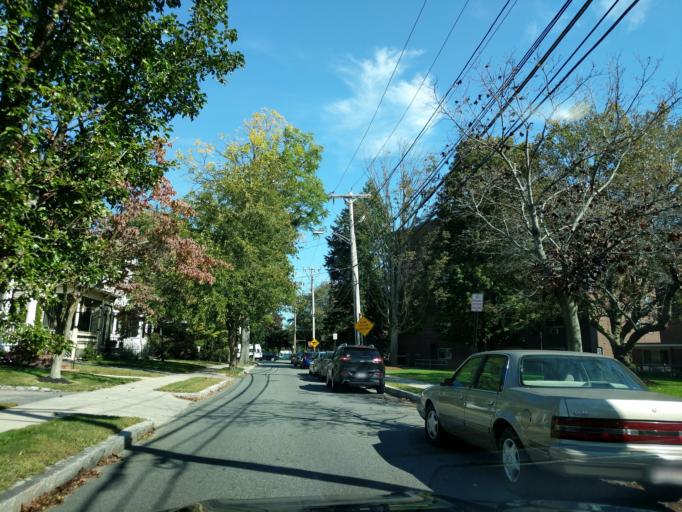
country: US
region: Massachusetts
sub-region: Middlesex County
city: Melrose
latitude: 42.4548
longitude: -71.0704
